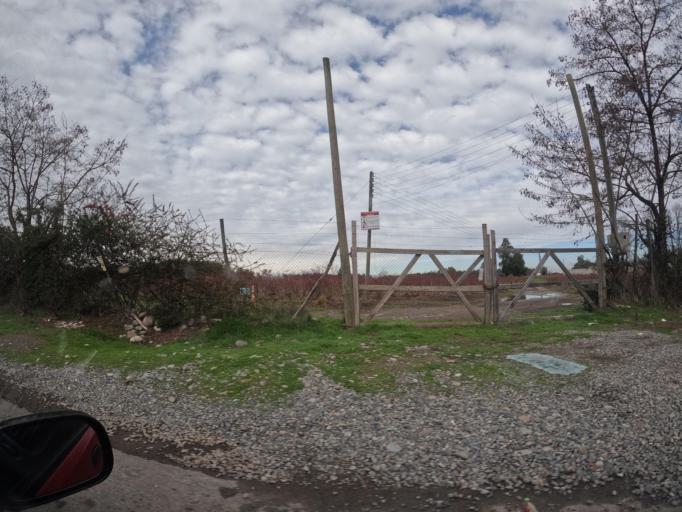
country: CL
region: Maule
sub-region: Provincia de Linares
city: Linares
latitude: -35.8653
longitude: -71.6217
